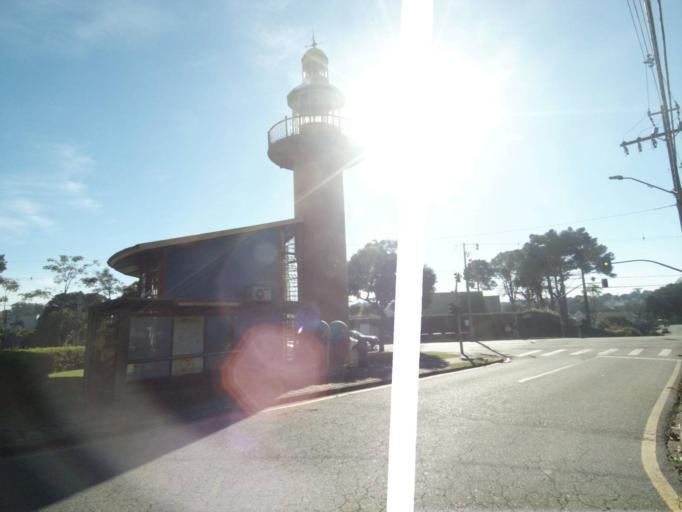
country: BR
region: Parana
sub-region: Curitiba
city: Curitiba
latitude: -25.4254
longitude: -49.3010
